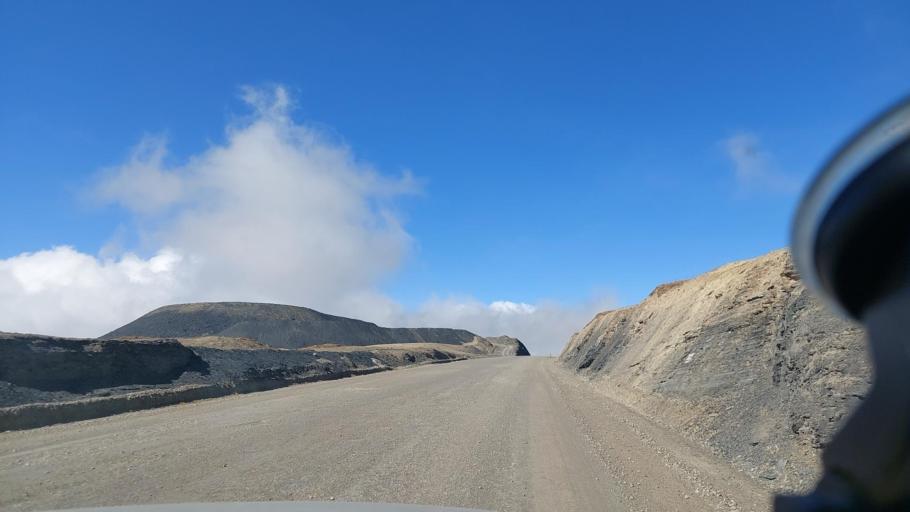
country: BO
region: La Paz
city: La Paz
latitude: -16.3428
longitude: -68.0553
